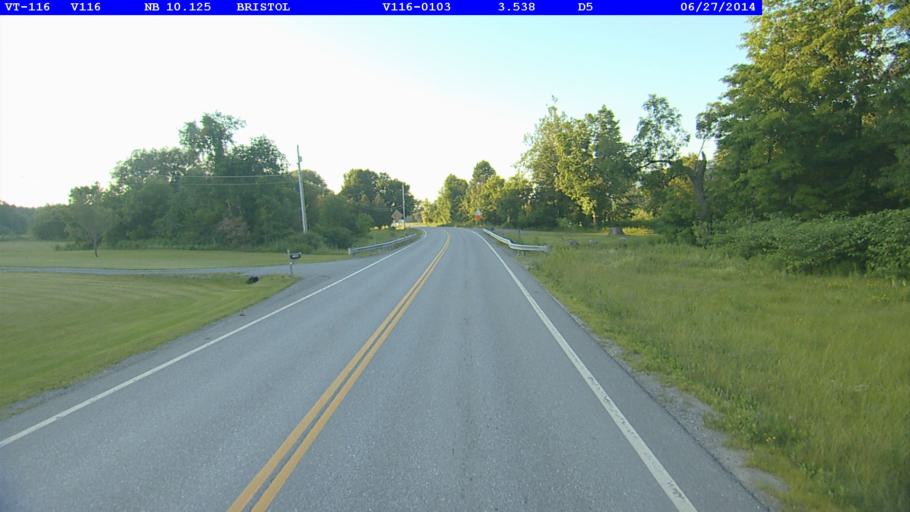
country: US
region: Vermont
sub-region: Addison County
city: Bristol
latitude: 44.1014
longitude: -73.0968
